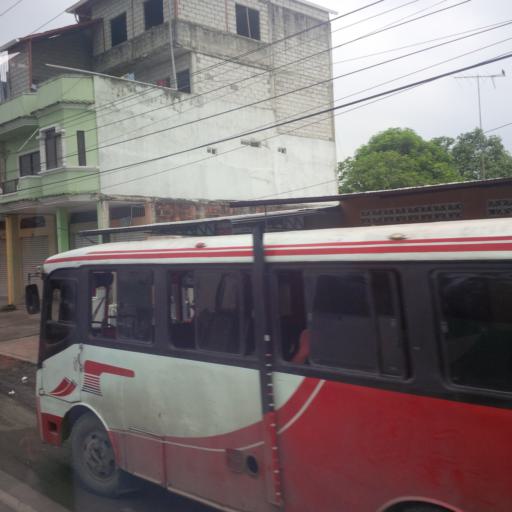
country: EC
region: Canar
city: La Troncal
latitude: -2.3364
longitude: -79.3945
